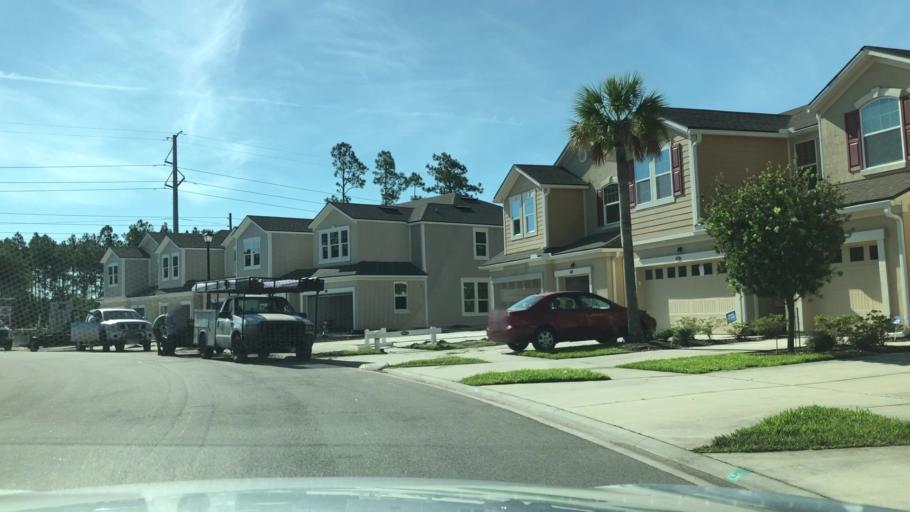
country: US
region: Florida
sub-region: Saint Johns County
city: Fruit Cove
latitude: 30.0700
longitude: -81.5332
